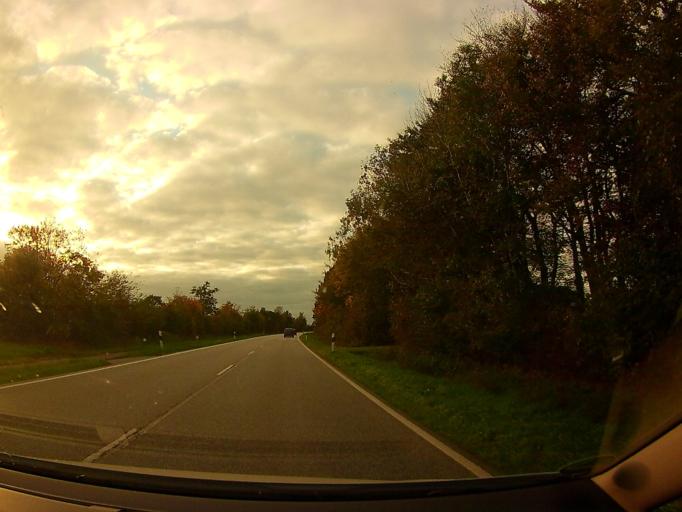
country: DE
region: Schleswig-Holstein
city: Silberstedt
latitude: 54.5157
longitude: 9.4119
